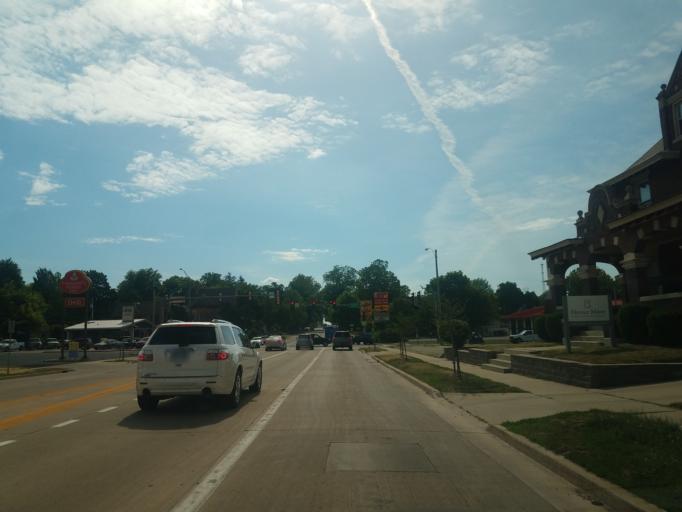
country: US
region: Illinois
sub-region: McLean County
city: Bloomington
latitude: 40.4798
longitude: -88.9837
